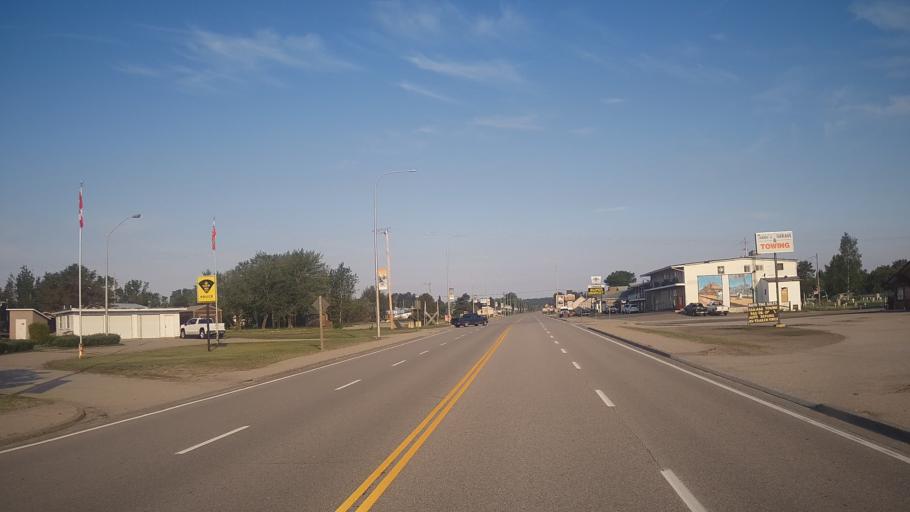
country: CA
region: Ontario
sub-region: Rainy River District
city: Atikokan
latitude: 49.4163
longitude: -91.6560
